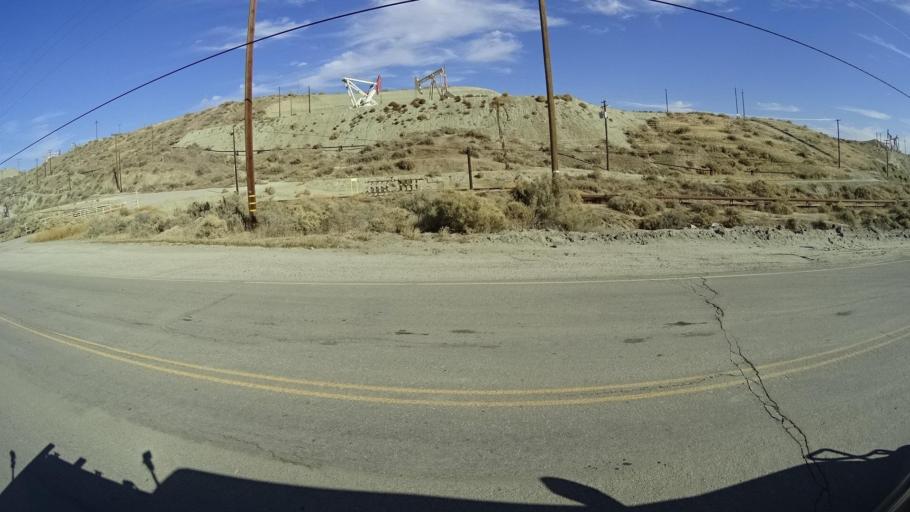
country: US
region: California
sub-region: Kern County
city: Oildale
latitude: 35.5699
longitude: -118.9585
